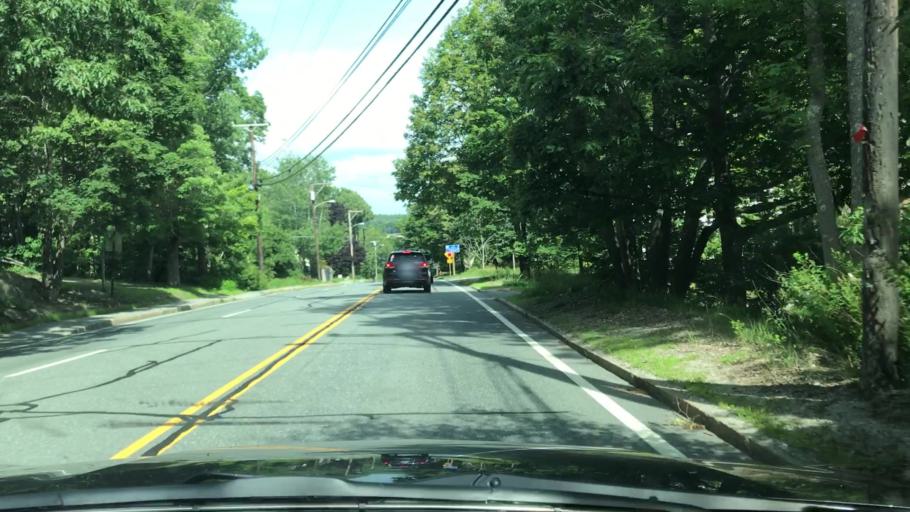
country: US
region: Maine
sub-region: Hancock County
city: Ellsworth
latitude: 44.5391
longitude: -68.4341
